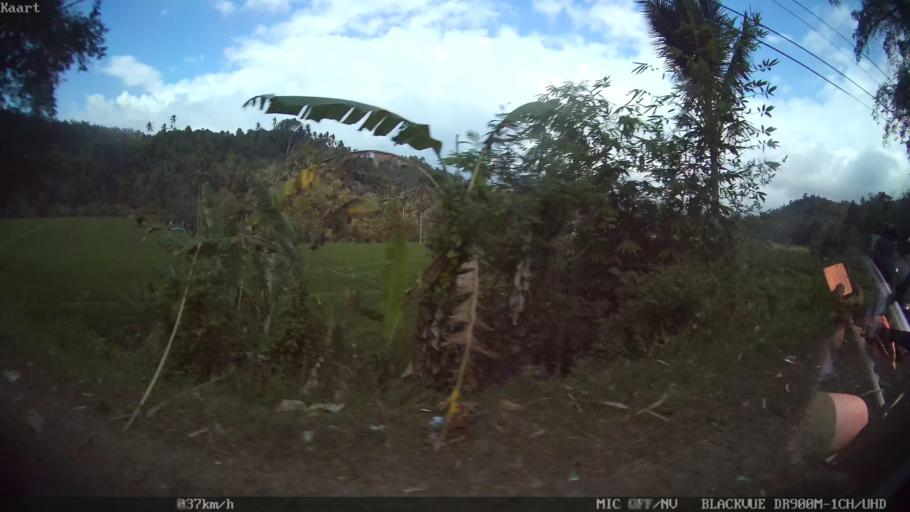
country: ID
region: Bali
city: Kauhan
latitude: -8.2762
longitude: 114.9707
